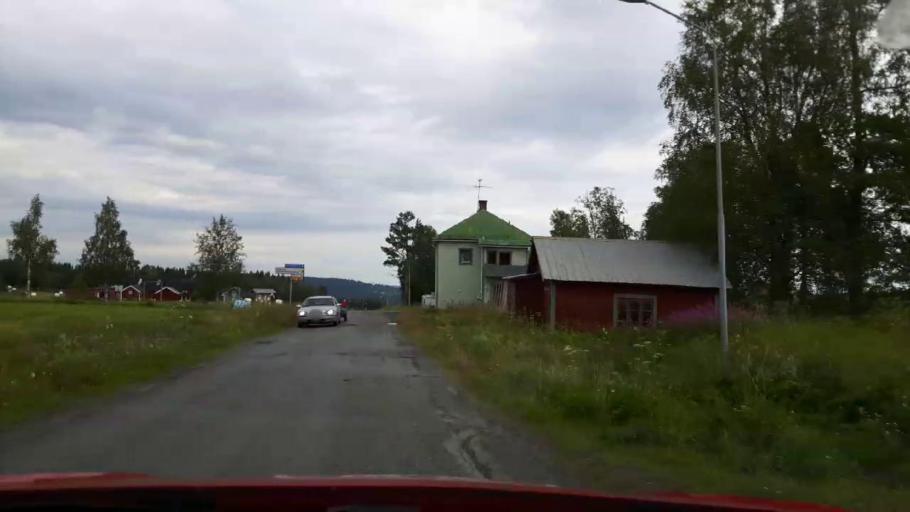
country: SE
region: Jaemtland
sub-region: Stroemsunds Kommun
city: Stroemsund
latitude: 63.5225
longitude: 15.3542
